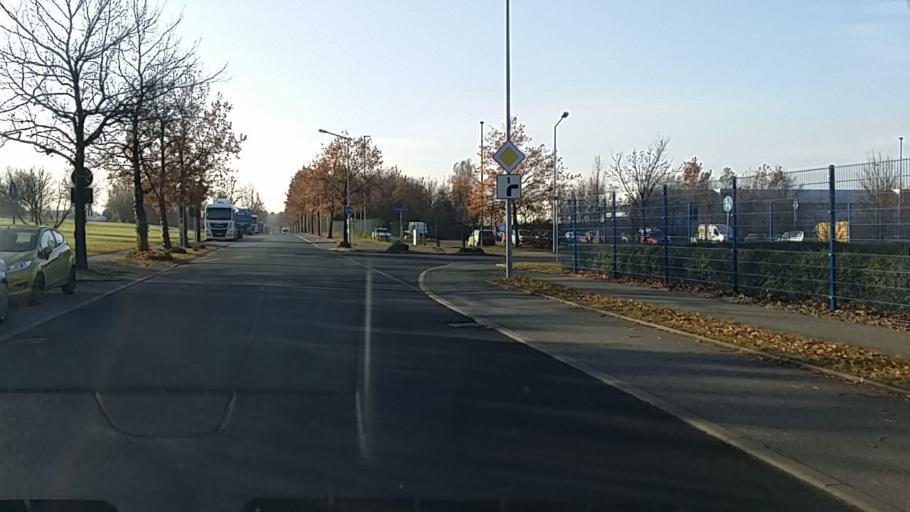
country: DE
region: Saxony
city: Ottendorf-Okrilla
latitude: 51.1776
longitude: 13.8388
